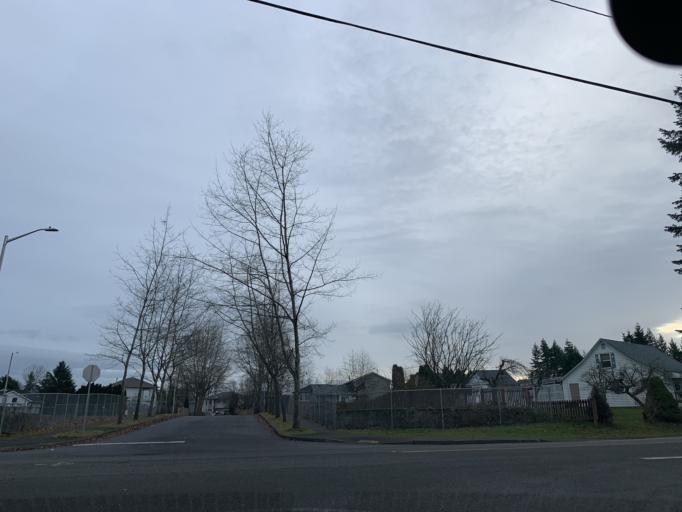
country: US
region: Washington
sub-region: Snohomish County
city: Marysville
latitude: 48.0880
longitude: -122.1624
